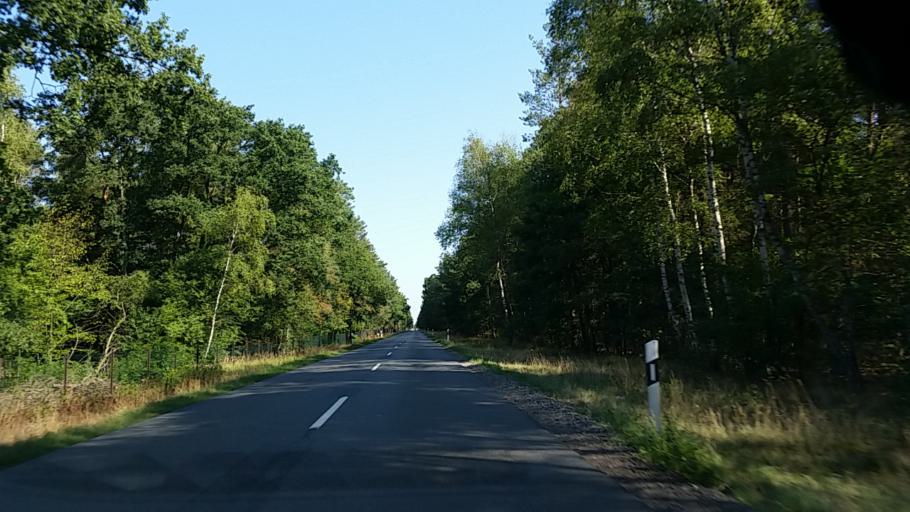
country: DE
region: Lower Saxony
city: Sassenburg
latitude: 52.5727
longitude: 10.6781
